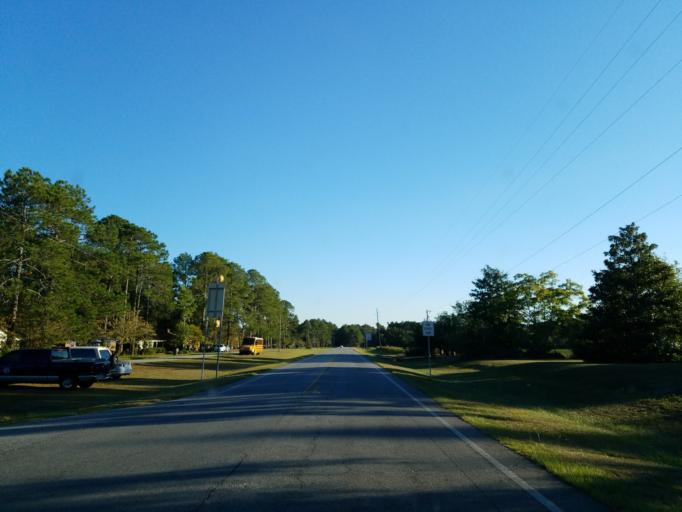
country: US
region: Georgia
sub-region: Worth County
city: Sylvester
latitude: 31.5447
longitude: -83.8431
